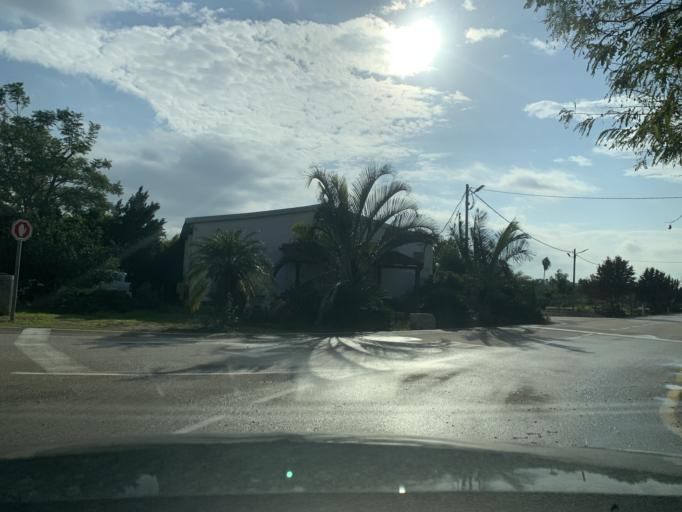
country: IL
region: Central District
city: Rosh Ha'Ayin
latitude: 32.0967
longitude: 34.9224
